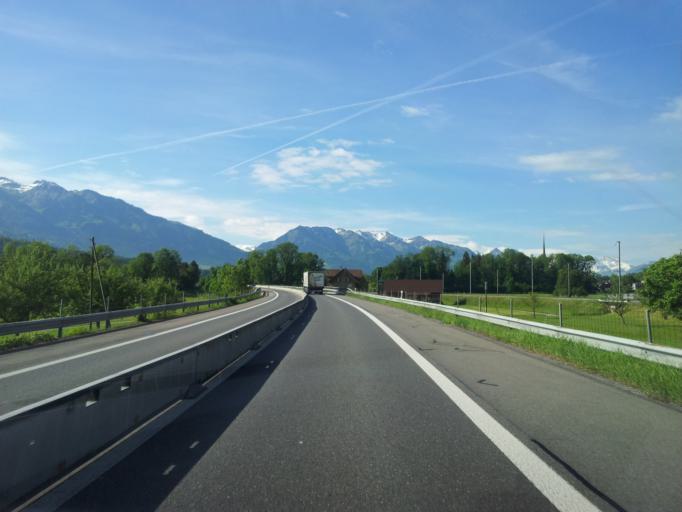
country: CH
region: Obwalden
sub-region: Obwalden
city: Alpnach
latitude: 46.9486
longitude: 8.2767
